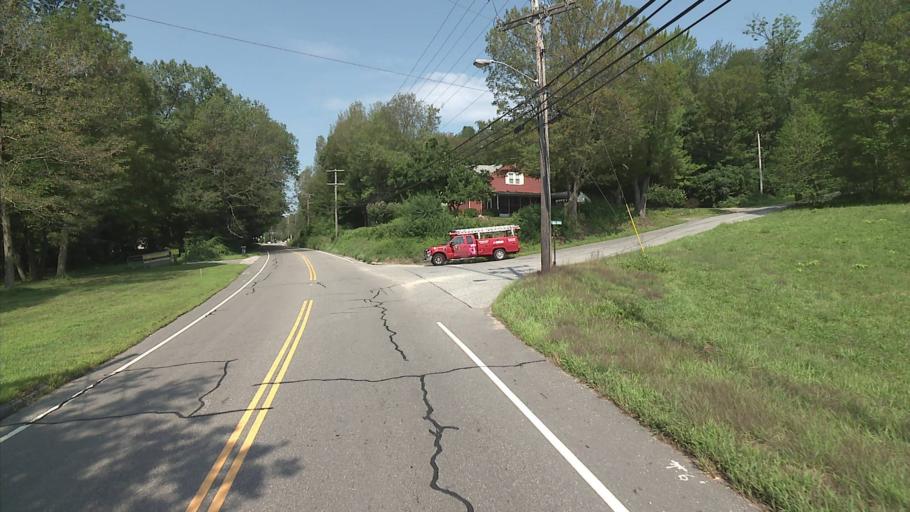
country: US
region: Connecticut
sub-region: New London County
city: Montville Center
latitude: 41.5647
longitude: -72.1613
